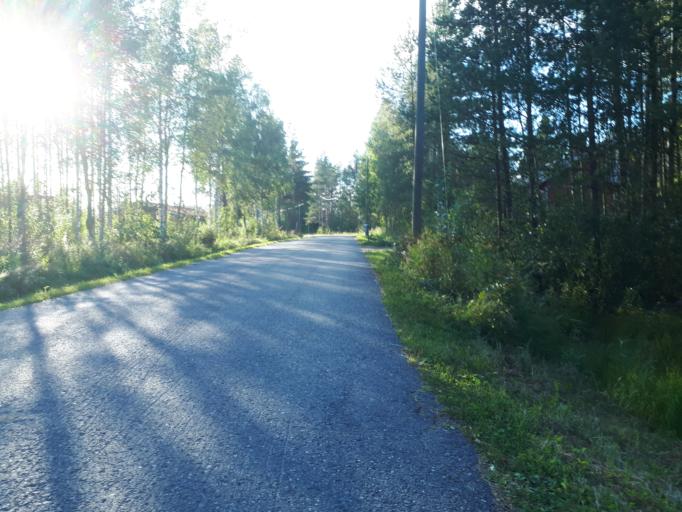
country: FI
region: Northern Ostrobothnia
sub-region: Oulunkaari
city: Ii
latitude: 65.3126
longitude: 25.3828
